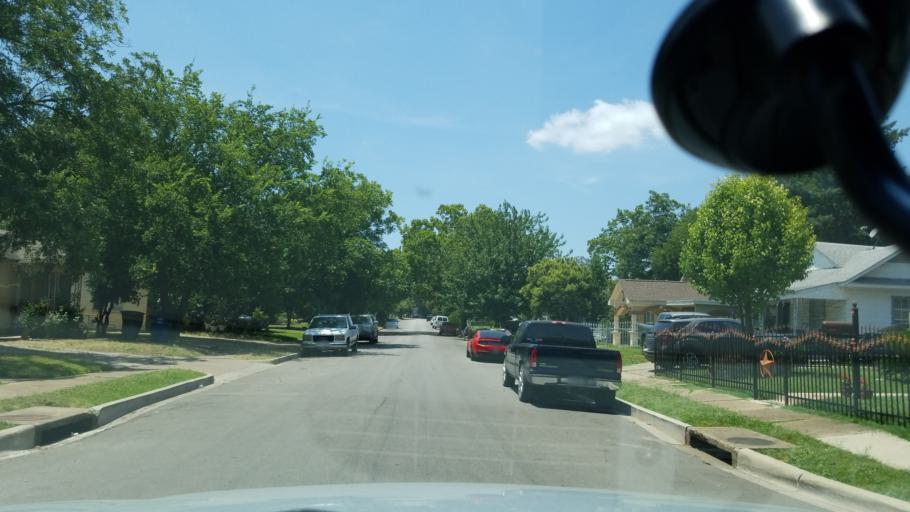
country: US
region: Texas
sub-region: Dallas County
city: Cockrell Hill
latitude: 32.7291
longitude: -96.8662
